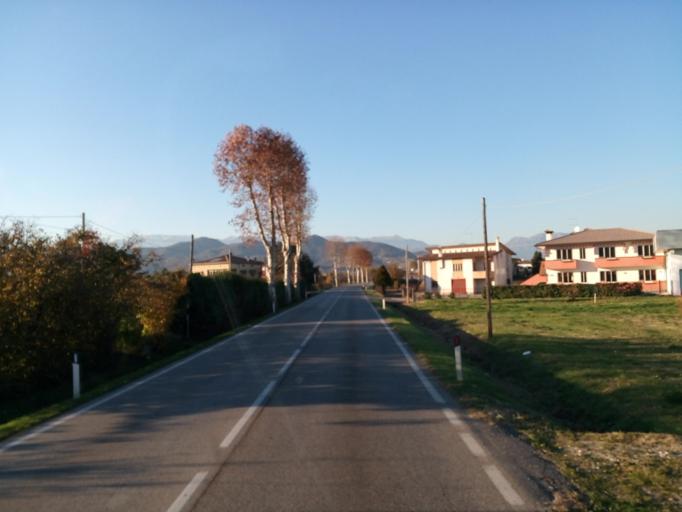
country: IT
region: Veneto
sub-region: Provincia di Treviso
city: Crocetta-Nogare
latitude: 45.8084
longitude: 12.0212
